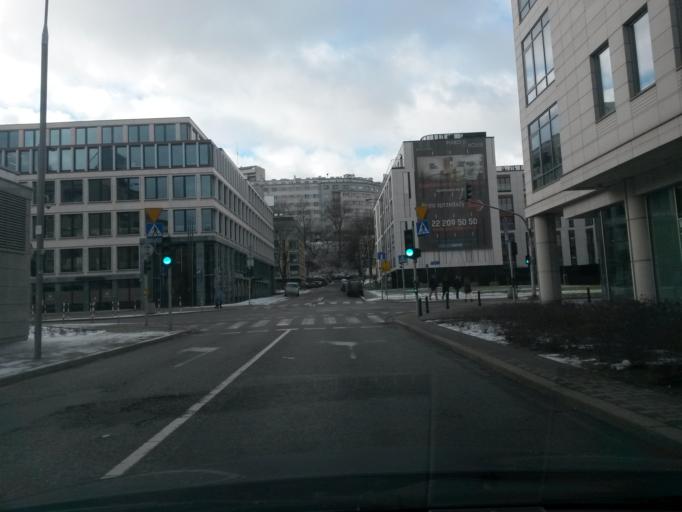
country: PL
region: Masovian Voivodeship
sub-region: Warszawa
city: Srodmiescie
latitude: 52.2385
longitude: 21.0257
